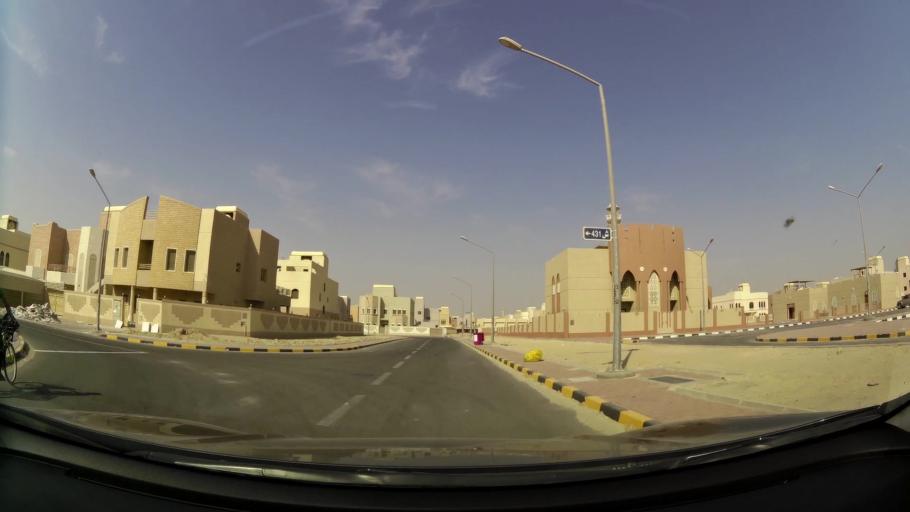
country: KW
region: Al Ahmadi
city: Al Wafrah
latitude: 28.7982
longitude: 48.0770
